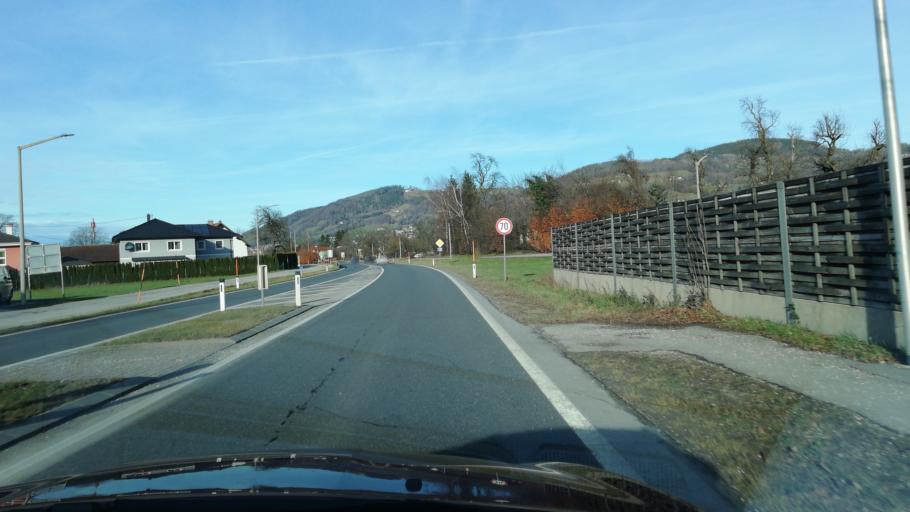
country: AT
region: Upper Austria
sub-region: Politischer Bezirk Kirchdorf an der Krems
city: Micheldorf in Oberoesterreich
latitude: 47.8796
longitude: 14.1284
